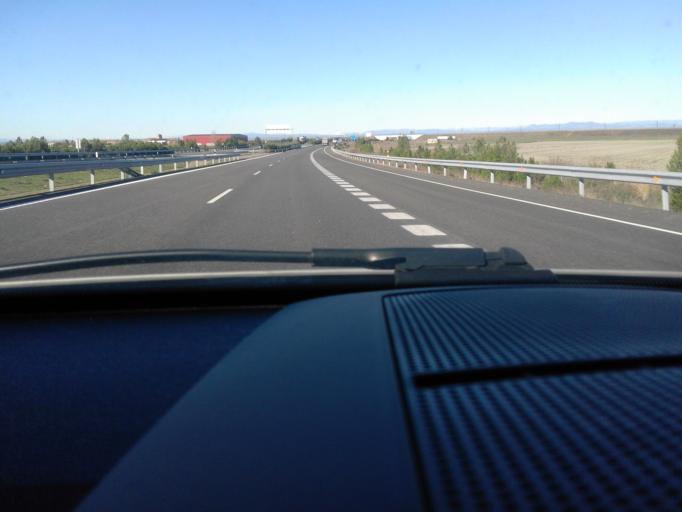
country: ES
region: Castille and Leon
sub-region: Provincia de Leon
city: Santas Martas
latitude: 42.4467
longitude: -5.3852
